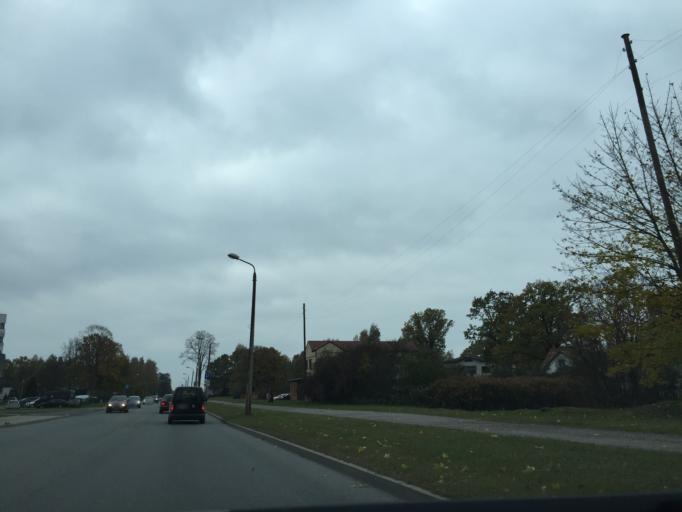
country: LV
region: Riga
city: Riga
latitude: 56.9110
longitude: 24.0958
